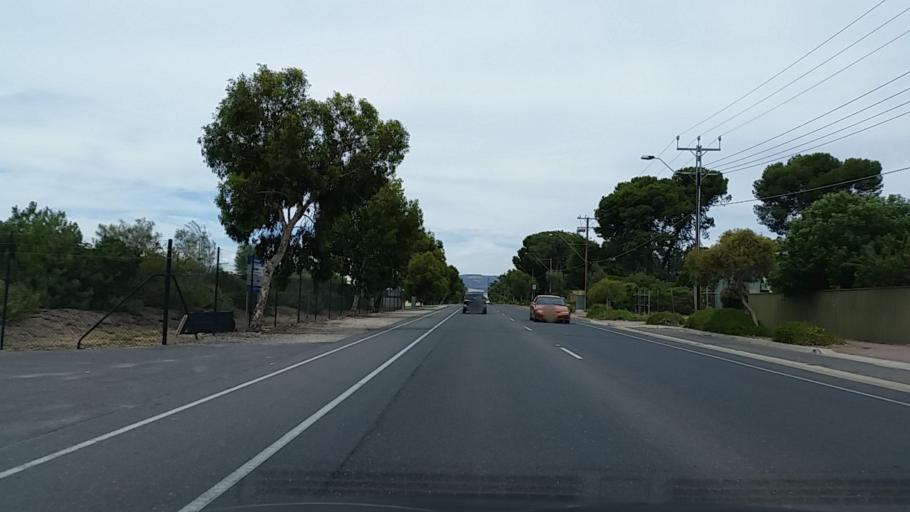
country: AU
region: South Australia
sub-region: Holdfast Bay
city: Glenelg East
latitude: -34.9583
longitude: 138.5302
